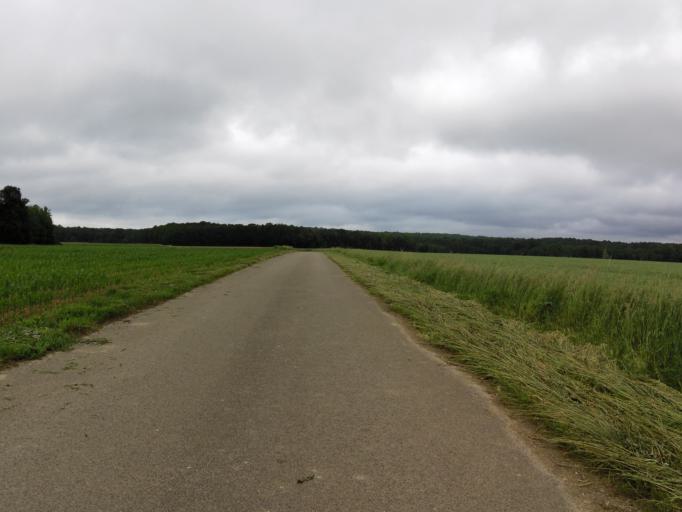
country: FR
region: Champagne-Ardenne
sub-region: Departement de la Haute-Marne
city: Montier-en-Der
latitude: 48.5164
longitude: 4.7744
